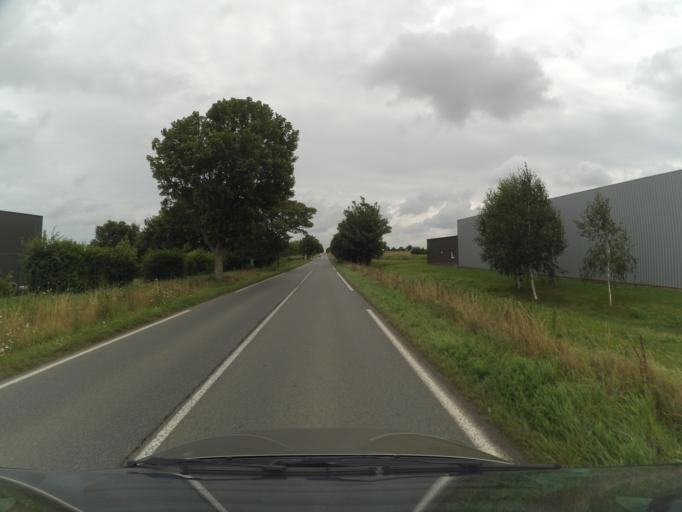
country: FR
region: Brittany
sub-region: Departement des Cotes-d'Armor
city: Tremuson
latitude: 48.5224
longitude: -2.8699
